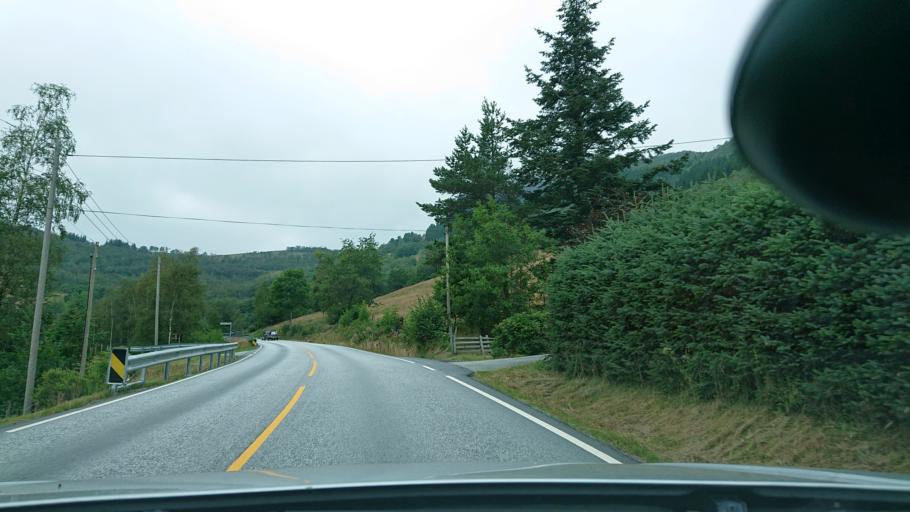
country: NO
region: Rogaland
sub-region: Hjelmeland
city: Hjelmelandsvagen
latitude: 59.1696
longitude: 6.1689
